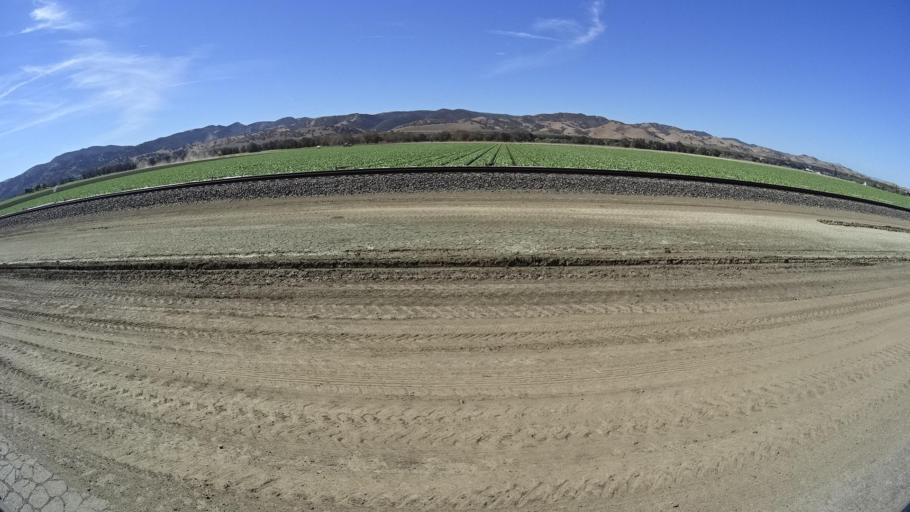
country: US
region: California
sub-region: San Luis Obispo County
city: Lake Nacimiento
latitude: 35.9976
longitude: -120.8845
